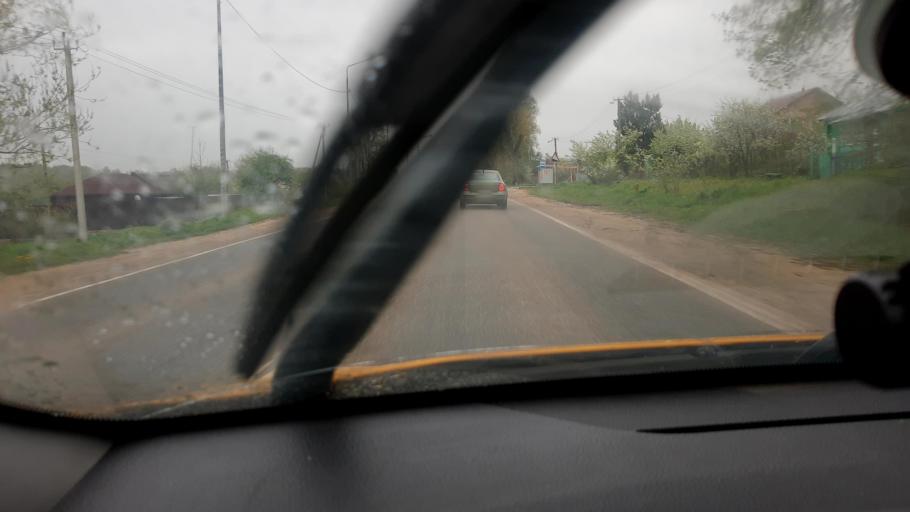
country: RU
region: Tula
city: Zaokskiy
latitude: 54.7619
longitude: 37.4371
